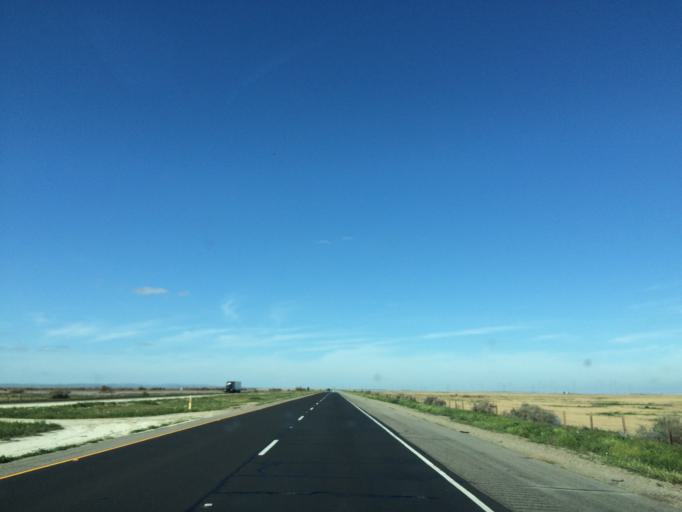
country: US
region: California
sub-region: Kern County
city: Lost Hills
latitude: 35.7967
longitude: -119.7874
